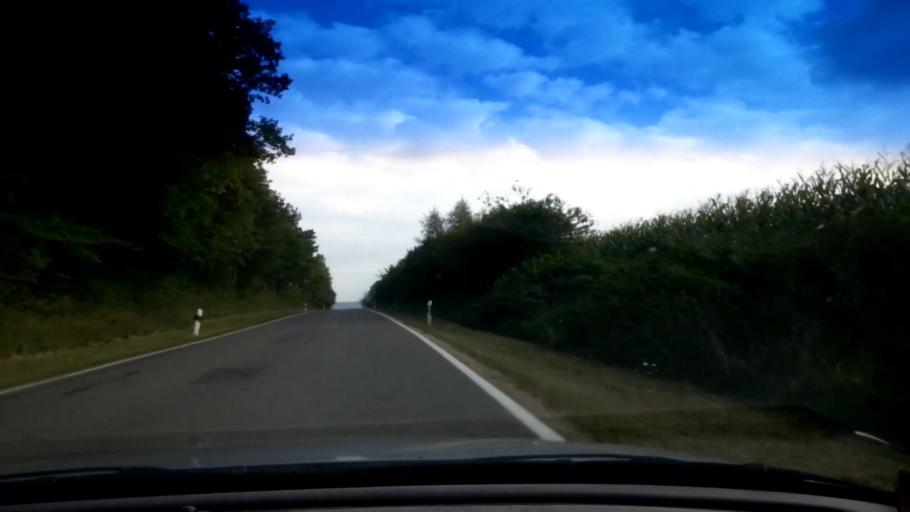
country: DE
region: Bavaria
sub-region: Upper Franconia
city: Memmelsdorf
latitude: 49.9772
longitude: 10.9690
